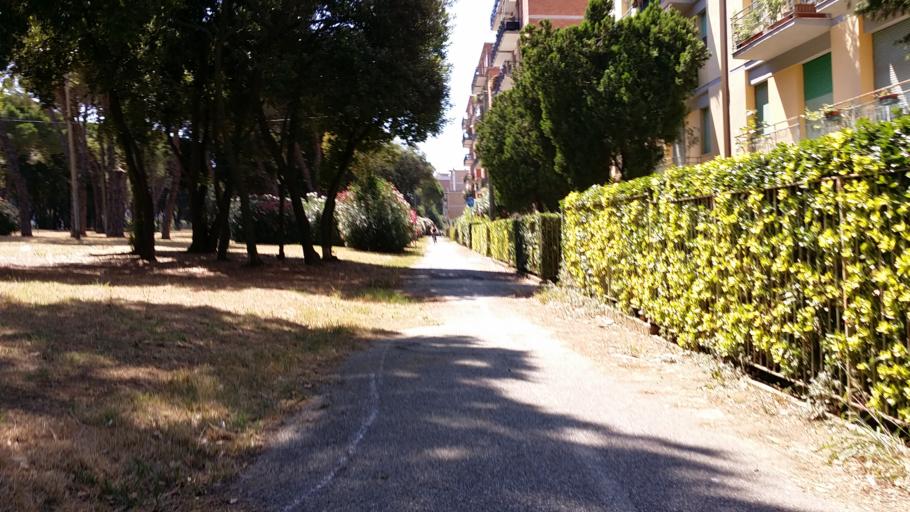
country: IT
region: Tuscany
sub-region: Provincia di Livorno
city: Livorno
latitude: 43.5461
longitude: 10.3304
